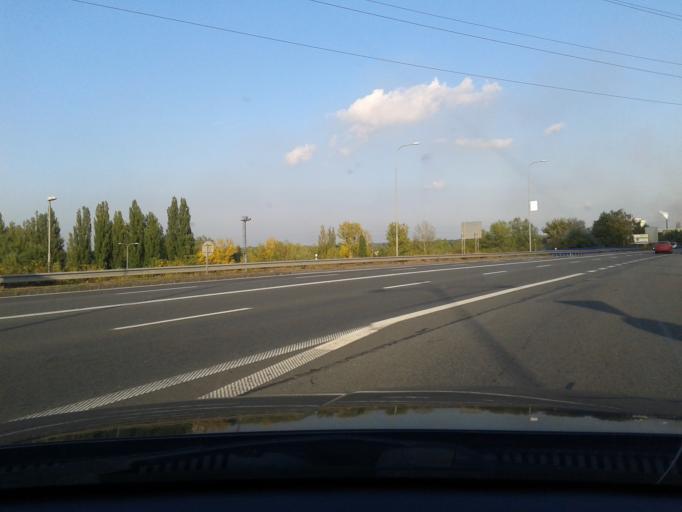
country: CZ
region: Moravskoslezsky
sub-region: Okres Ostrava-Mesto
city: Ostrava
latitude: 49.8063
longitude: 18.2798
